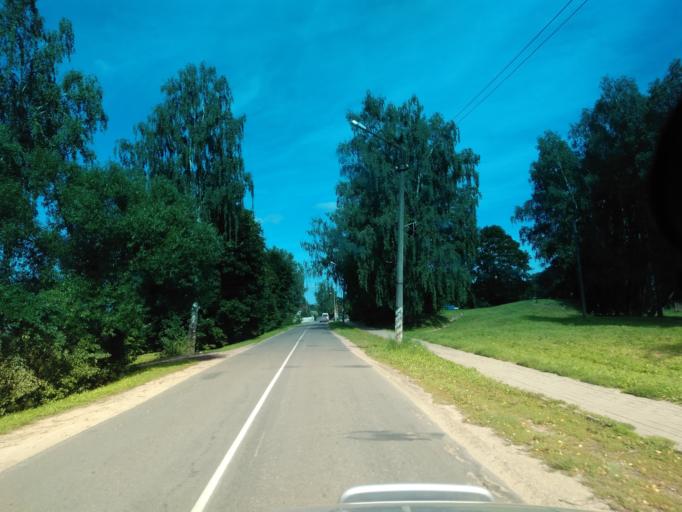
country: BY
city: Fanipol
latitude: 53.7436
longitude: 27.3298
